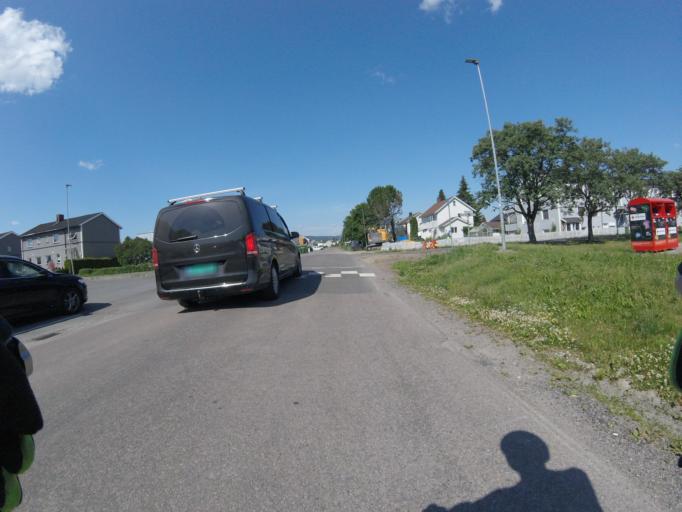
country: NO
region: Akershus
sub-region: Skedsmo
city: Lillestrom
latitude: 59.9609
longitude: 11.0462
